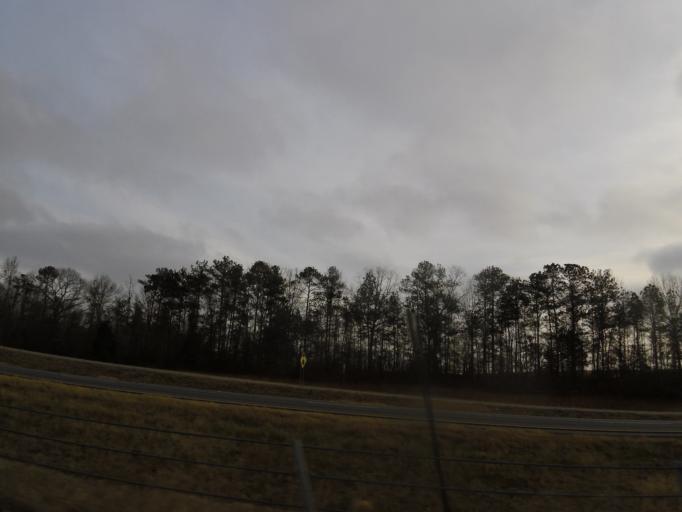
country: US
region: Alabama
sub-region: Autauga County
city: Marbury
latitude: 32.7346
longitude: -86.5415
